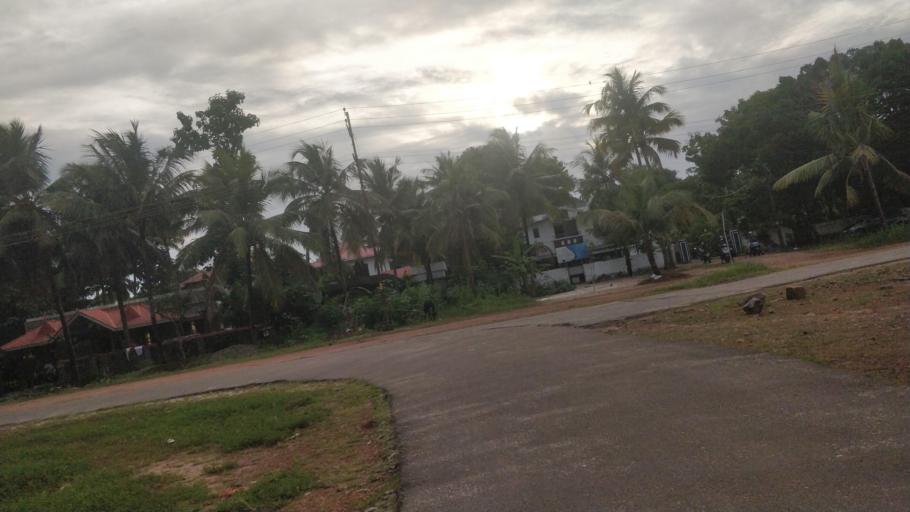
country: IN
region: Kerala
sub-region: Alappuzha
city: Shertallai
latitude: 9.6950
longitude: 76.3615
